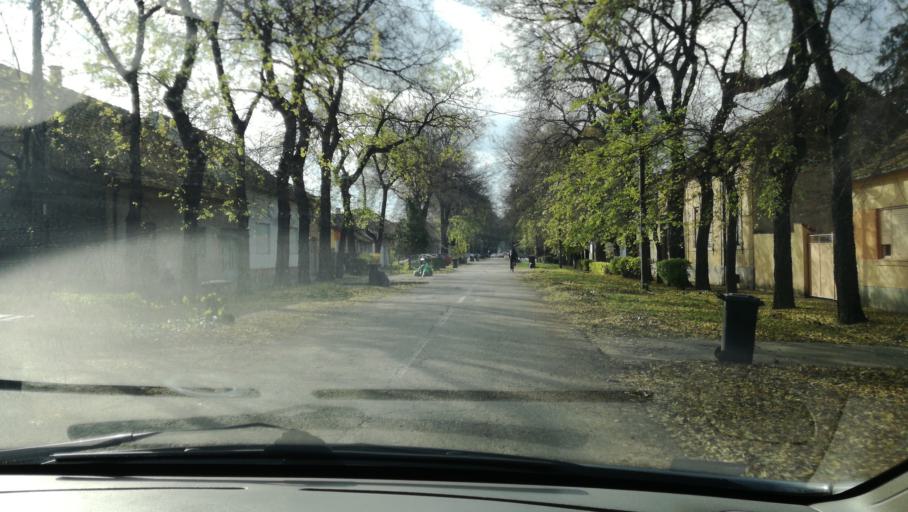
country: RS
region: Autonomna Pokrajina Vojvodina
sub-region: Severnobanatski Okrug
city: Kikinda
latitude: 45.8341
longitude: 20.4745
